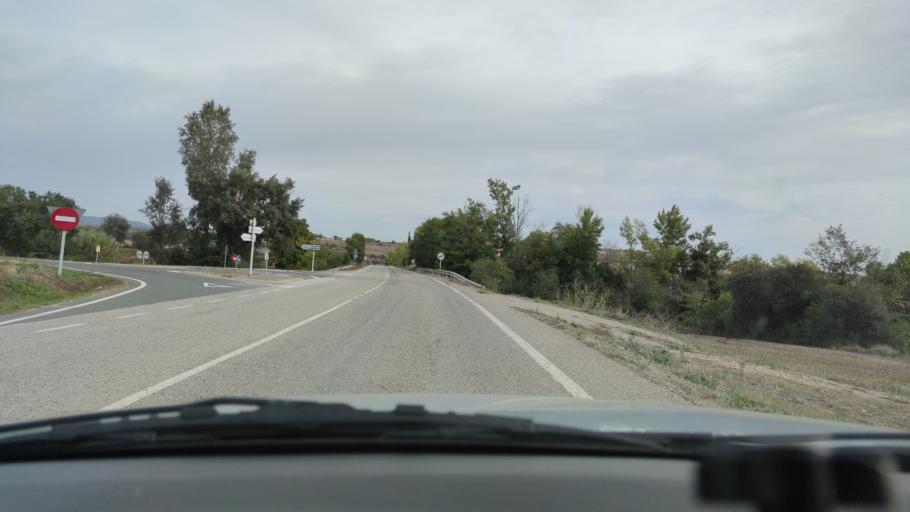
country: ES
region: Catalonia
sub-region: Provincia de Lleida
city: Artesa de Segre
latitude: 41.9179
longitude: 1.0745
